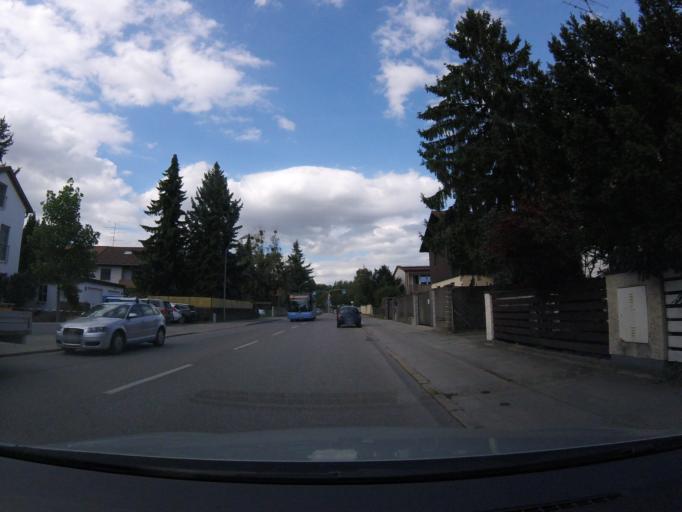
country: DE
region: Bavaria
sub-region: Upper Bavaria
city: Bogenhausen
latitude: 48.1421
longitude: 11.6382
